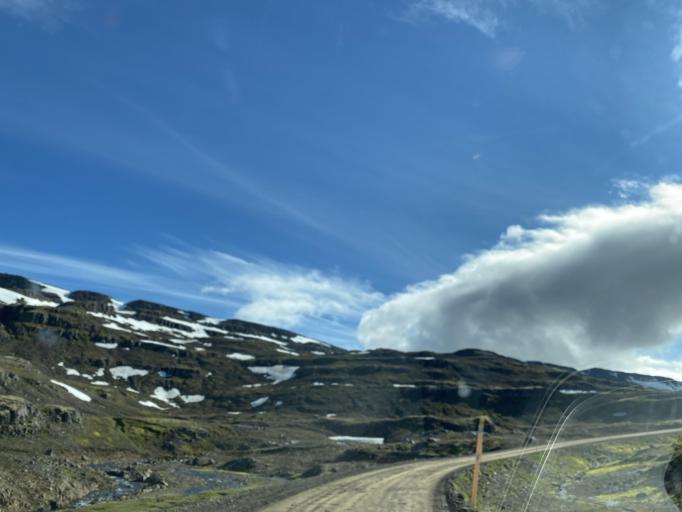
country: IS
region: East
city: Eskifjoerdur
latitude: 65.1702
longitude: -14.1210
